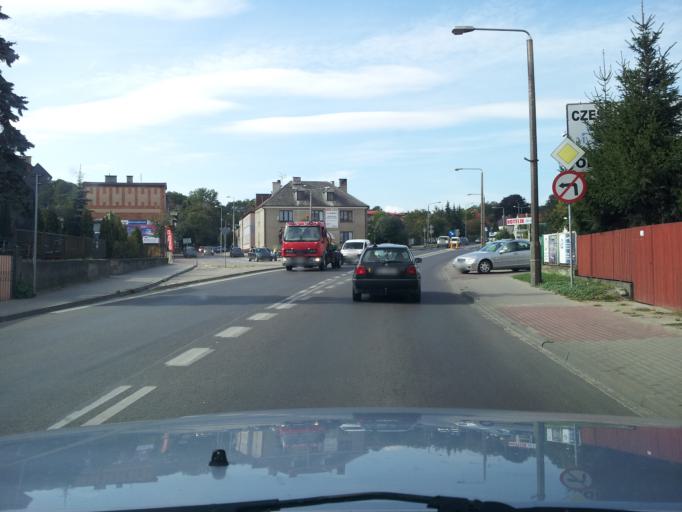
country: PL
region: Warmian-Masurian Voivodeship
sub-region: Powiat nowomiejski
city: Nowe Miasto Lubawskie
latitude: 53.4236
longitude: 19.5900
